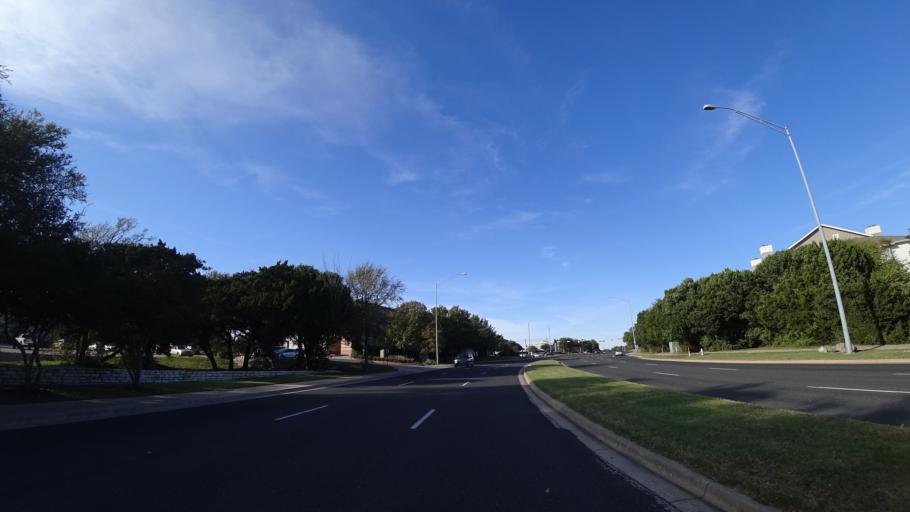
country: US
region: Texas
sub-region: Williamson County
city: Jollyville
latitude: 30.3892
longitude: -97.7393
